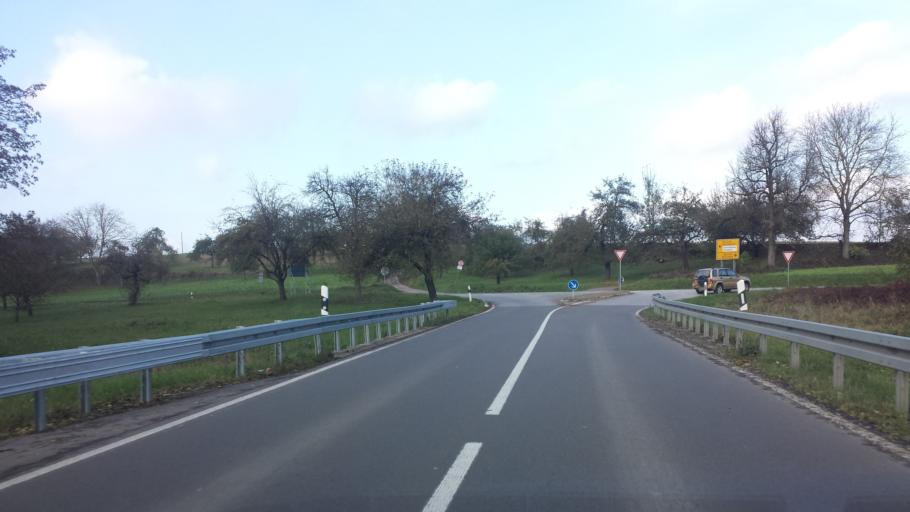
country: DE
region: Baden-Wuerttemberg
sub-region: Karlsruhe Region
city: Zaisenhausen
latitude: 49.1192
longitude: 8.7408
